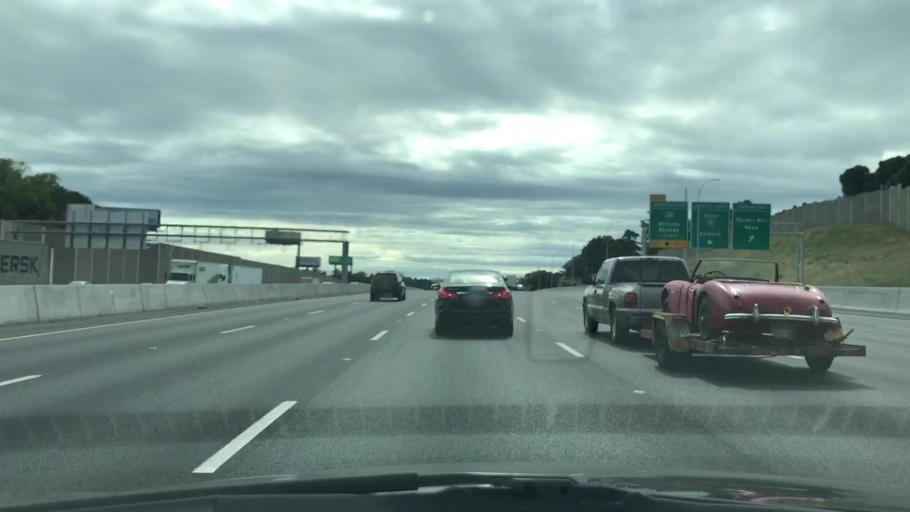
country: US
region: Georgia
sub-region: Cobb County
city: Smyrna
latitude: 33.9186
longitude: -84.4819
